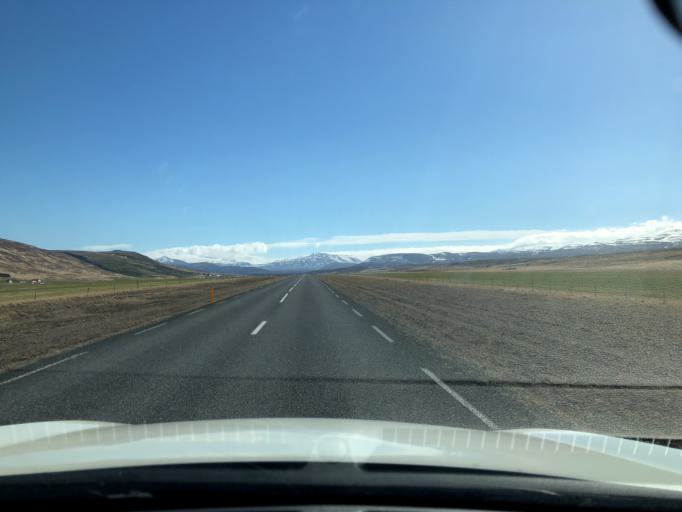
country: IS
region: South
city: Hveragerdi
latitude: 64.7027
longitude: -21.1441
